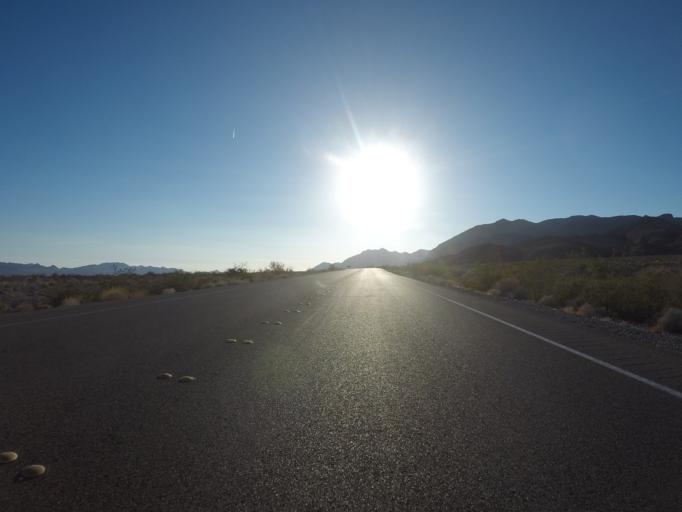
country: US
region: Nevada
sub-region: Clark County
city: Moapa Valley
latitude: 36.3803
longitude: -114.4380
